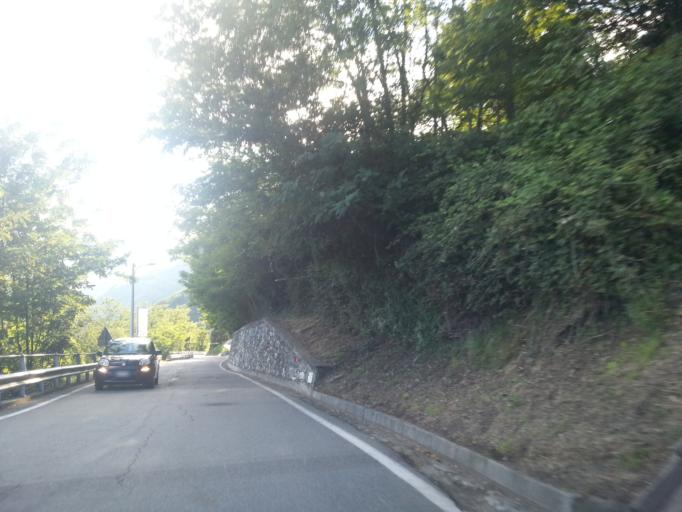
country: IT
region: Lombardy
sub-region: Provincia di Como
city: Montemezzo
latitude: 46.1748
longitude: 9.3753
